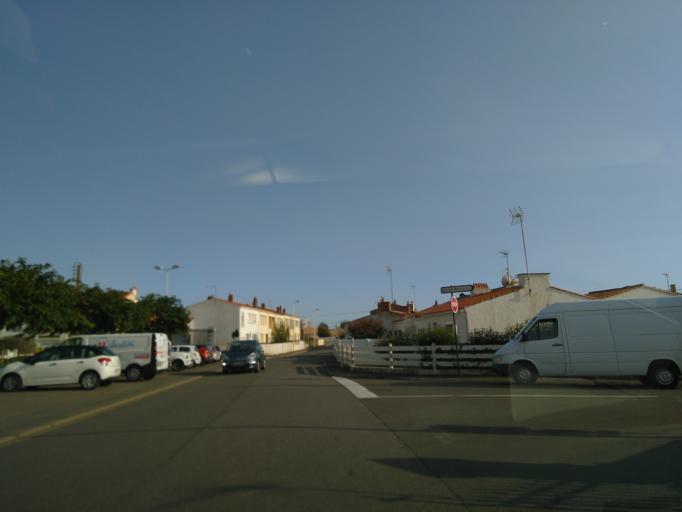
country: FR
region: Pays de la Loire
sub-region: Departement de la Vendee
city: Les Sables-d'Olonne
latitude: 46.4994
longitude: -1.8031
